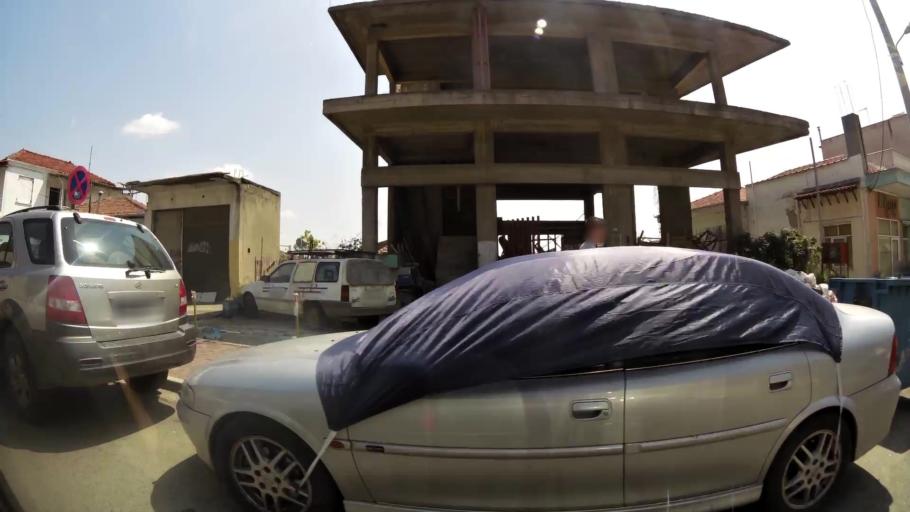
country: GR
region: Central Macedonia
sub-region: Nomos Imathias
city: Veroia
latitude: 40.5161
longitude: 22.2062
